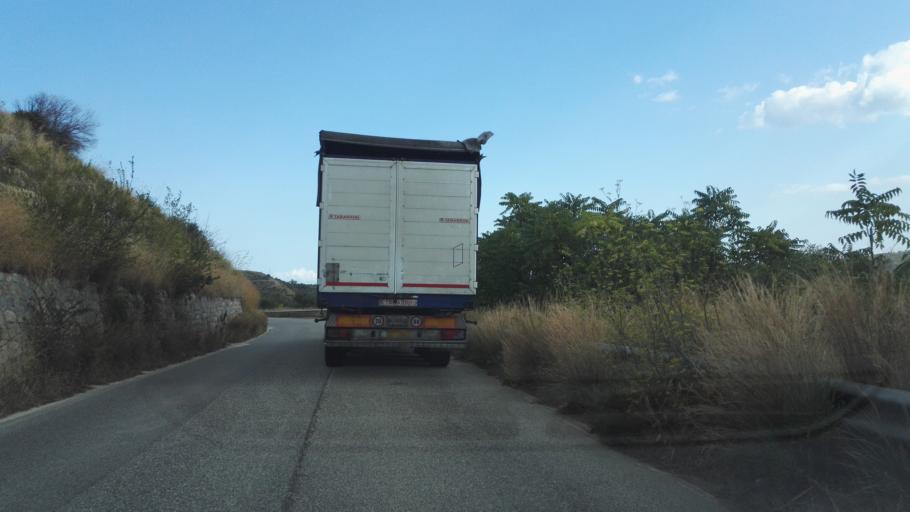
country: IT
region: Calabria
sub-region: Provincia di Reggio Calabria
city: Monasterace
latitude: 38.4633
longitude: 16.5156
